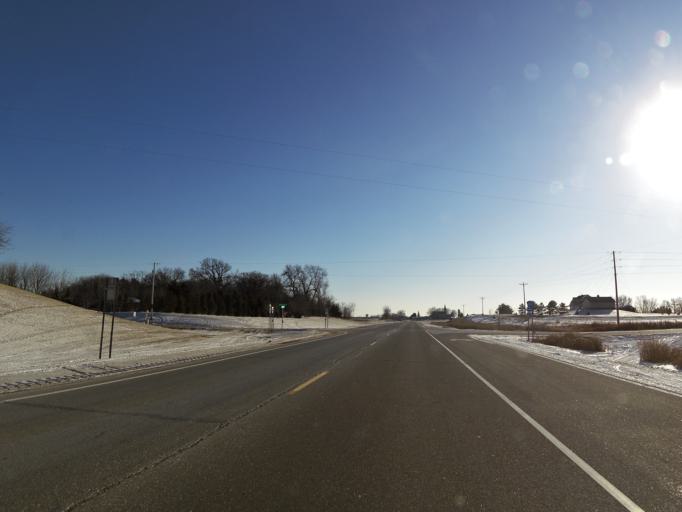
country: US
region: Minnesota
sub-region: Le Sueur County
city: New Prague
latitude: 44.6024
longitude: -93.5014
